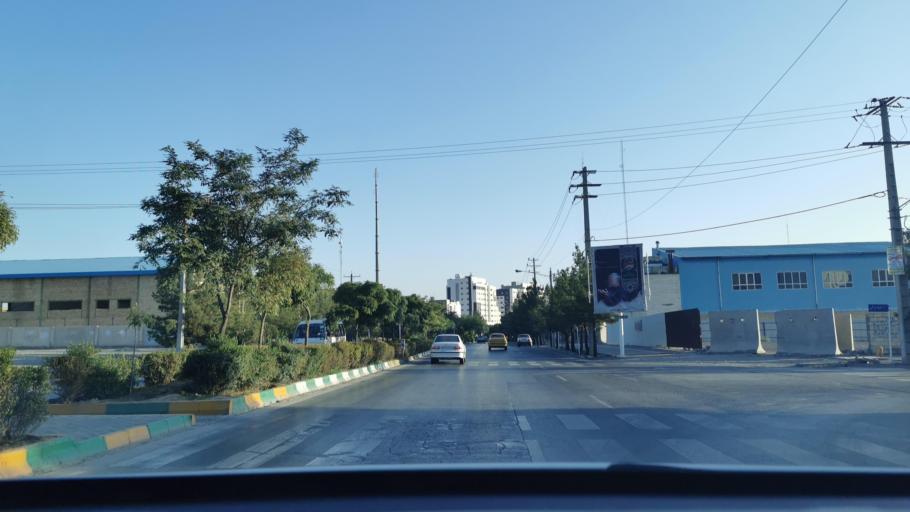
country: IR
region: Razavi Khorasan
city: Mashhad
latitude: 36.3565
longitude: 59.5130
